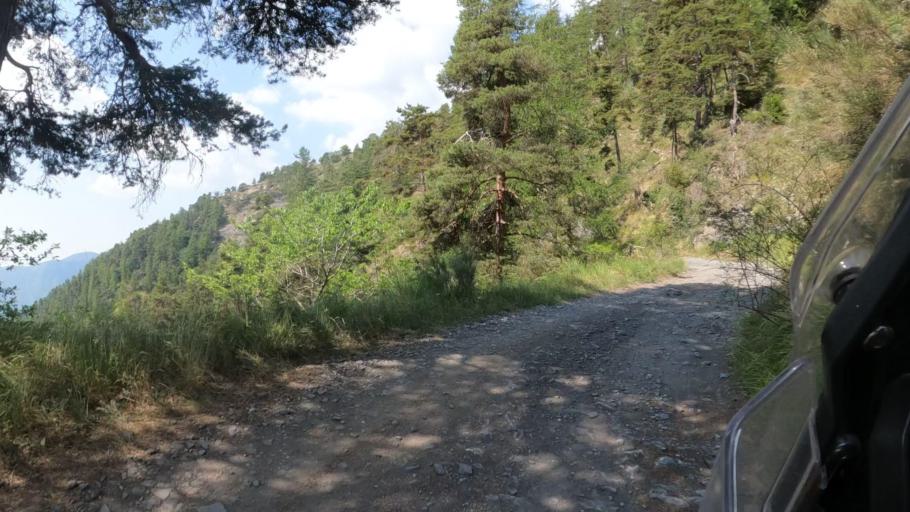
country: IT
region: Piedmont
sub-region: Provincia di Cuneo
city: Briga Alta
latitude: 44.0427
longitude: 7.7031
